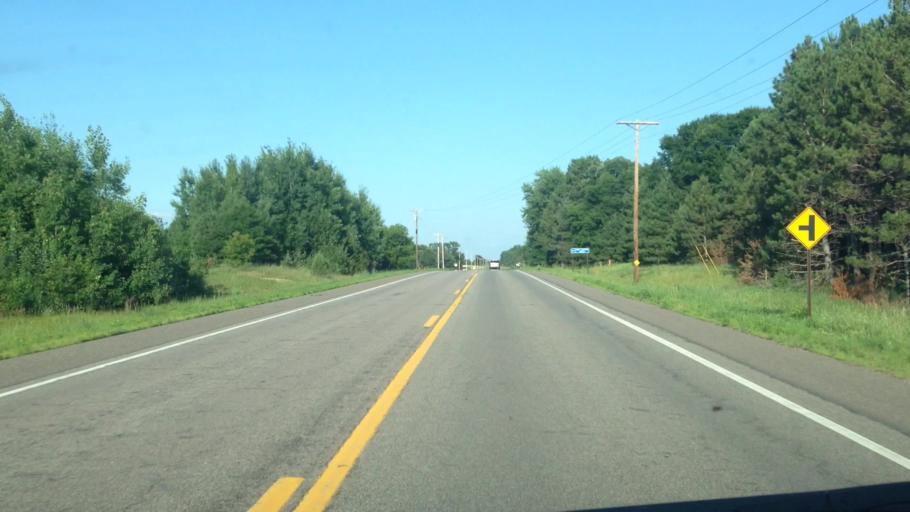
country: US
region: Minnesota
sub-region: Sherburne County
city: Big Lake
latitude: 45.4477
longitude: -93.7287
